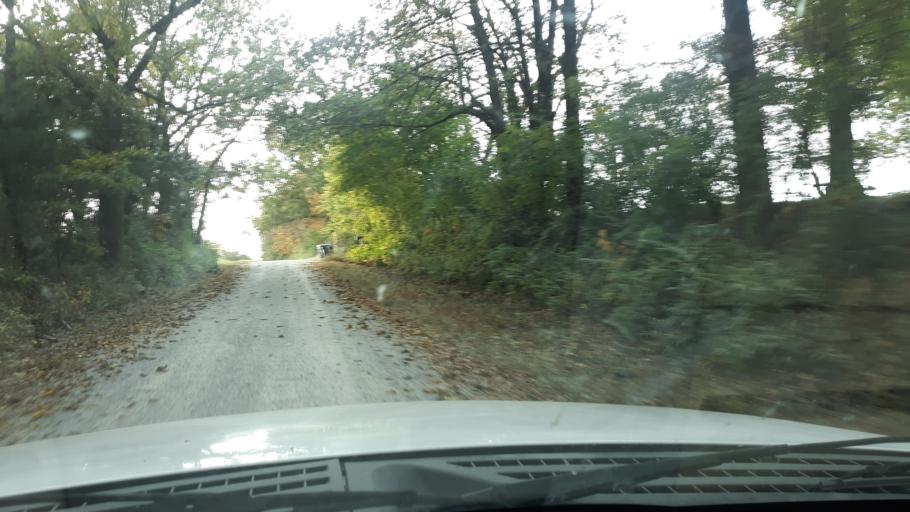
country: US
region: Illinois
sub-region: Saline County
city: Eldorado
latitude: 37.8343
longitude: -88.5014
